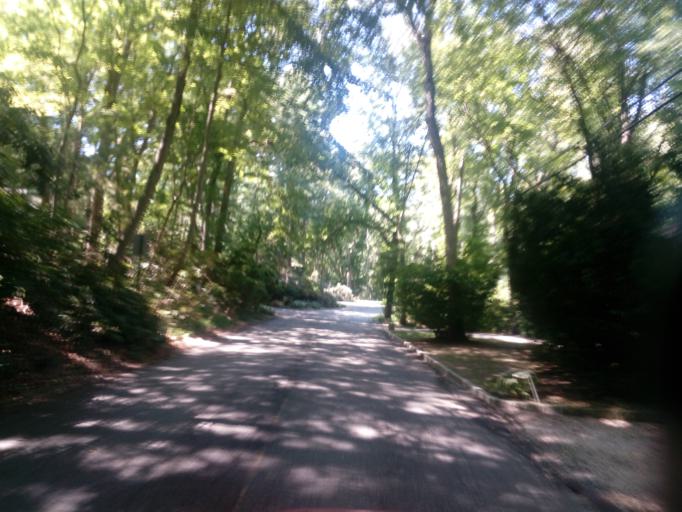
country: US
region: New York
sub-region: Nassau County
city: Upper Brookville
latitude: 40.8448
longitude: -73.5696
